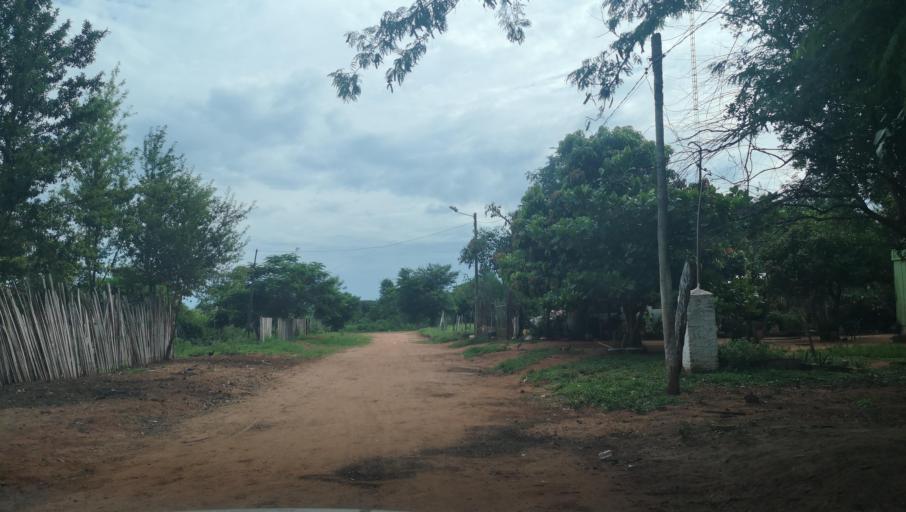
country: PY
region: San Pedro
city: Capiibary
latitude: -24.7214
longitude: -56.0196
